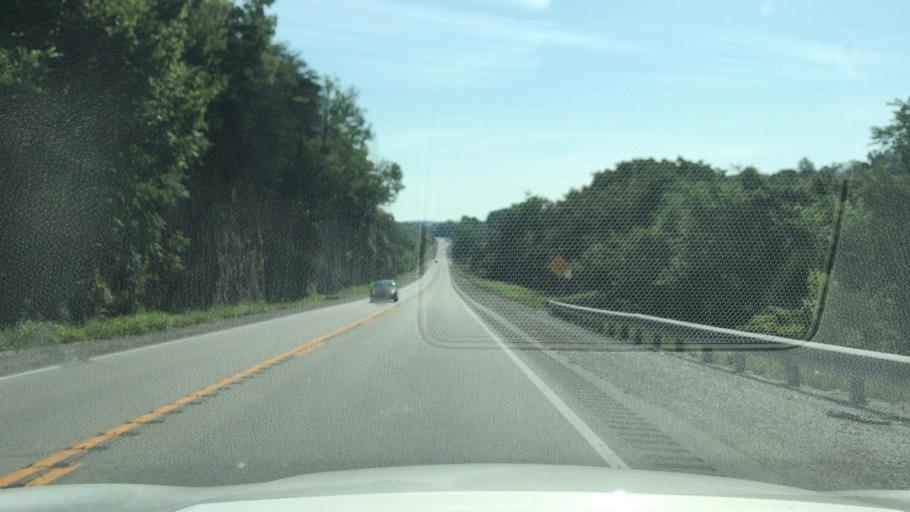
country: US
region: Kentucky
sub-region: Wayne County
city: Monticello
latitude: 36.7643
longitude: -84.9798
